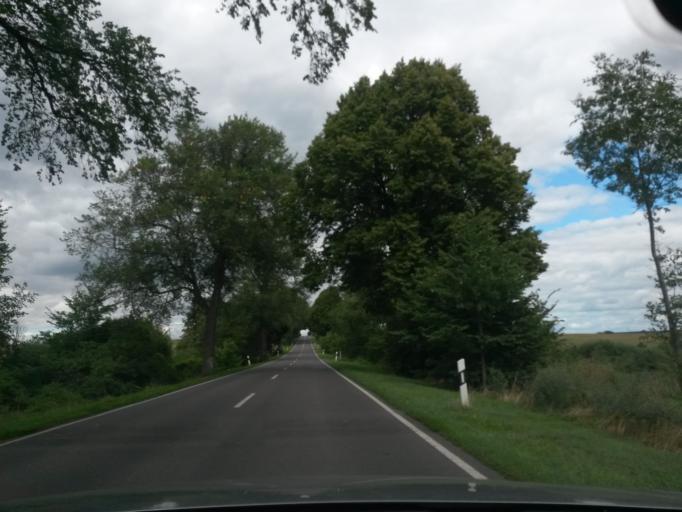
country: DE
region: Brandenburg
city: Angermunde
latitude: 52.9621
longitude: 13.9594
